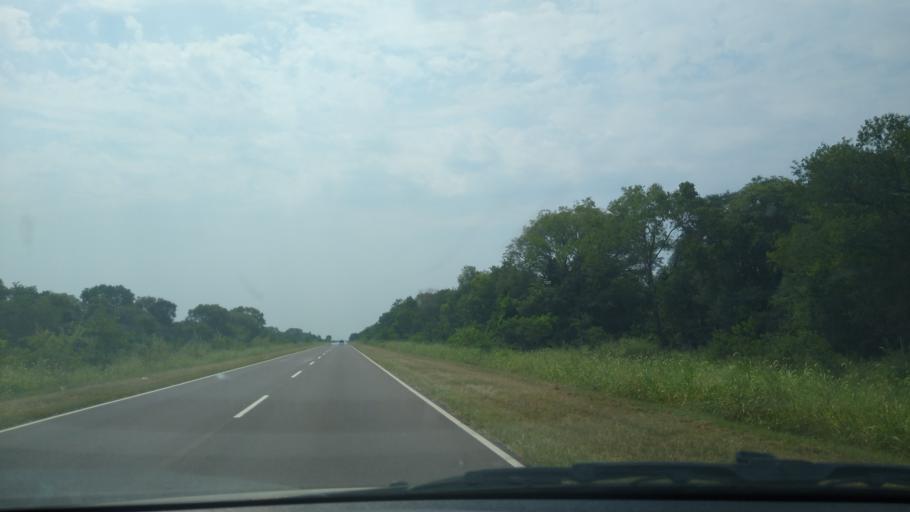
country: AR
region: Chaco
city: La Eduvigis
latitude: -27.0135
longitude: -58.9697
